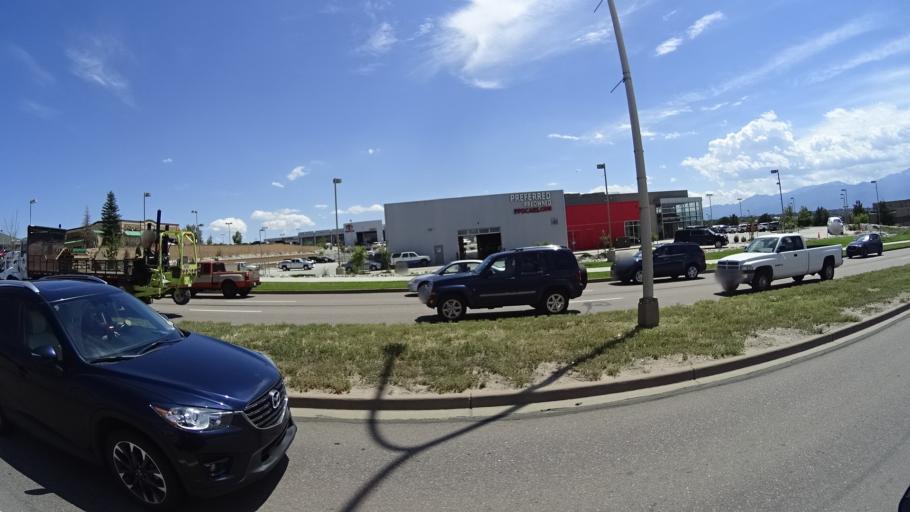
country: US
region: Colorado
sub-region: El Paso County
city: Black Forest
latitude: 38.9403
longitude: -104.7313
